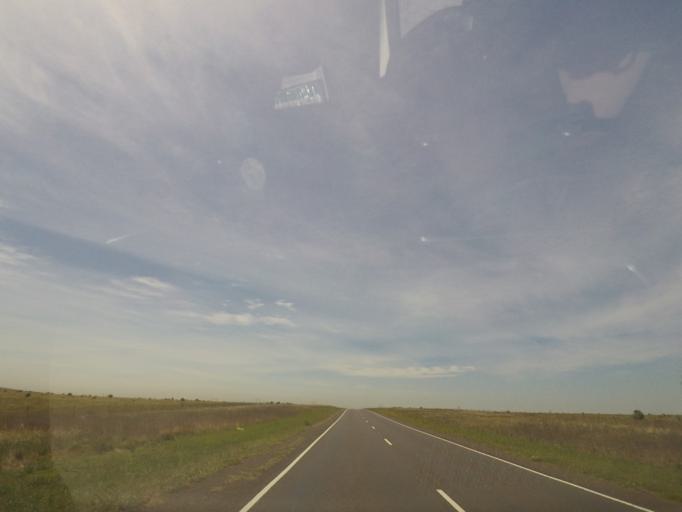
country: AU
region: Victoria
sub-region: Wyndham
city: Wyndham Vale
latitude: -37.8067
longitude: 144.5015
